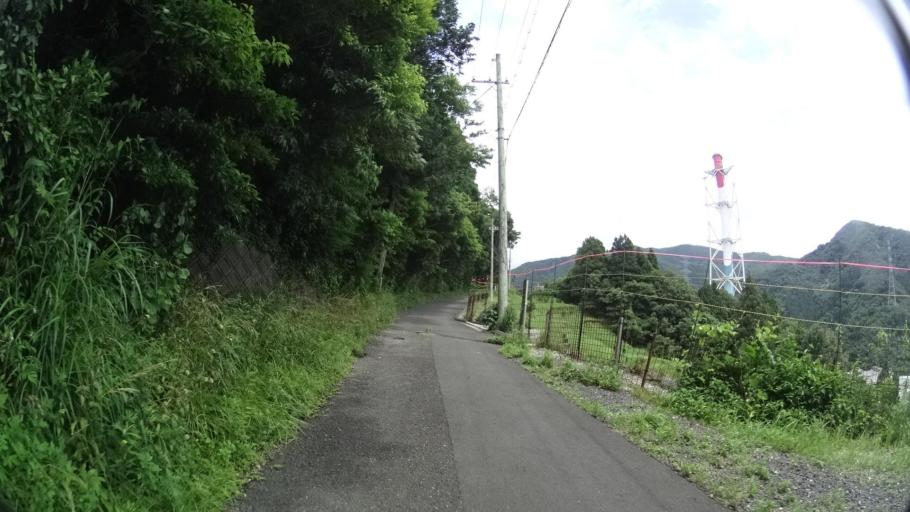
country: JP
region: Kyoto
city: Maizuru
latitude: 35.5320
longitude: 135.3417
